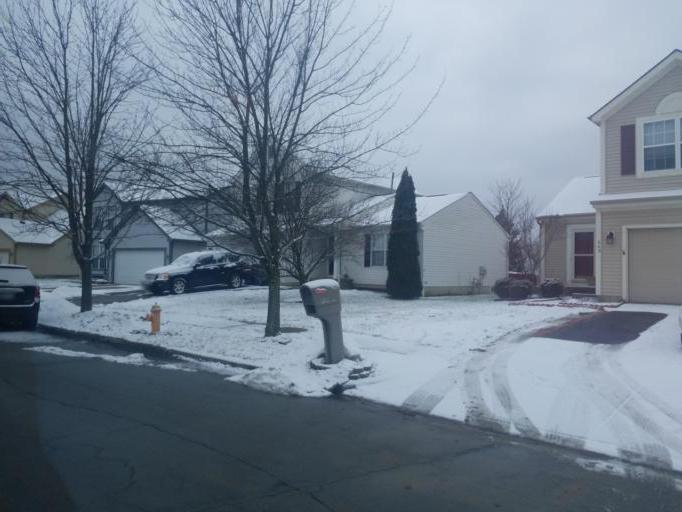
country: US
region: Ohio
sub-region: Franklin County
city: Reynoldsburg
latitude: 39.9953
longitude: -82.7828
